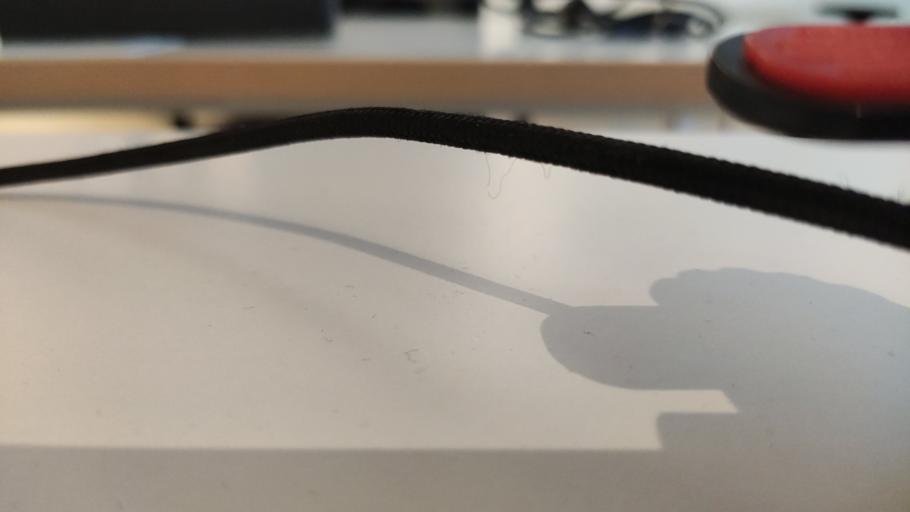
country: RU
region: Moskovskaya
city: Novopetrovskoye
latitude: 55.8654
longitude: 36.3910
